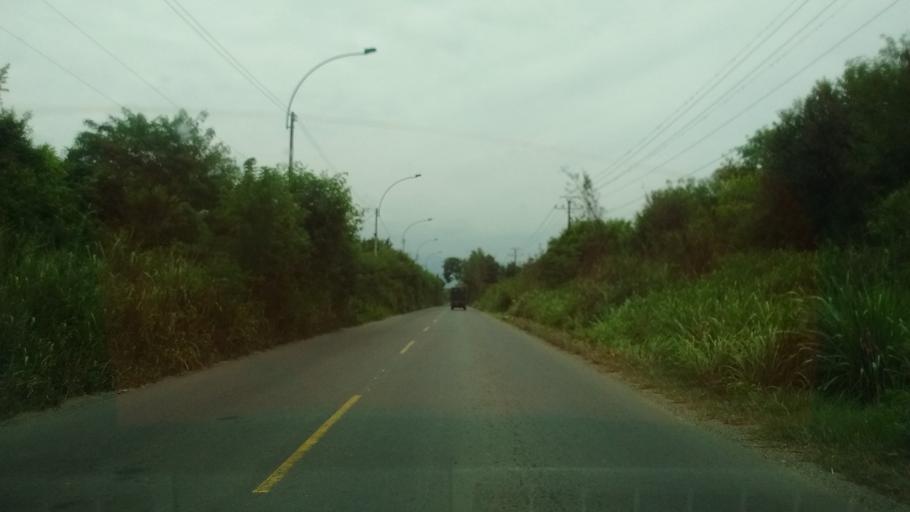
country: CO
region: Valle del Cauca
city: Jamundi
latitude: 3.3317
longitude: -76.5097
